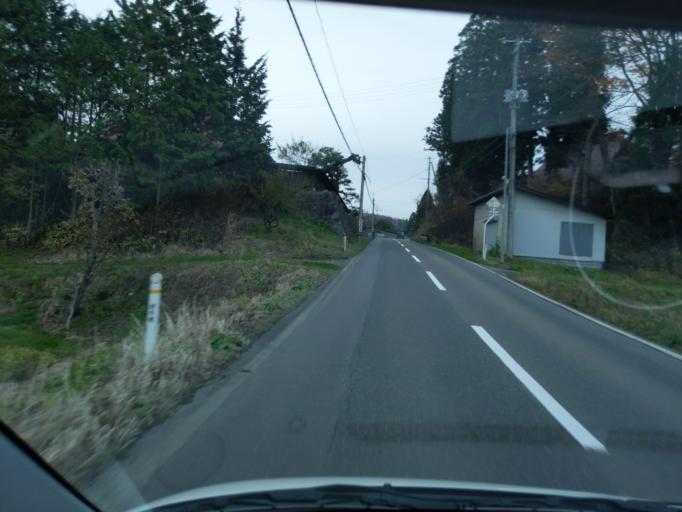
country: JP
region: Iwate
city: Kitakami
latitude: 39.2288
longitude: 141.2466
